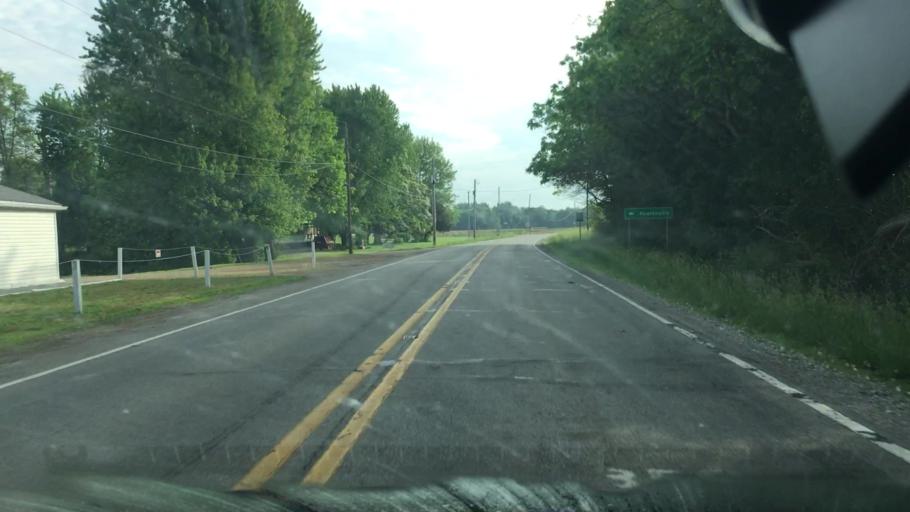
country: US
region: Kentucky
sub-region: Hancock County
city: Lewisport
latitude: 37.9451
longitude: -86.9735
